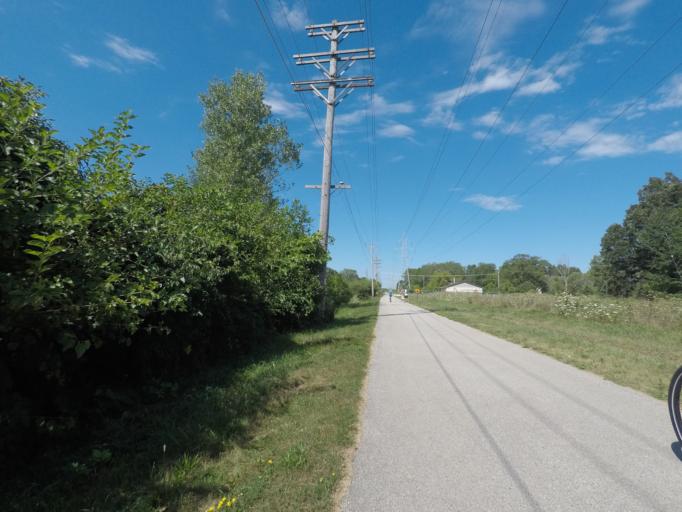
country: US
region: Wisconsin
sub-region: Waukesha County
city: Waukesha
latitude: 43.0099
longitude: -88.1846
